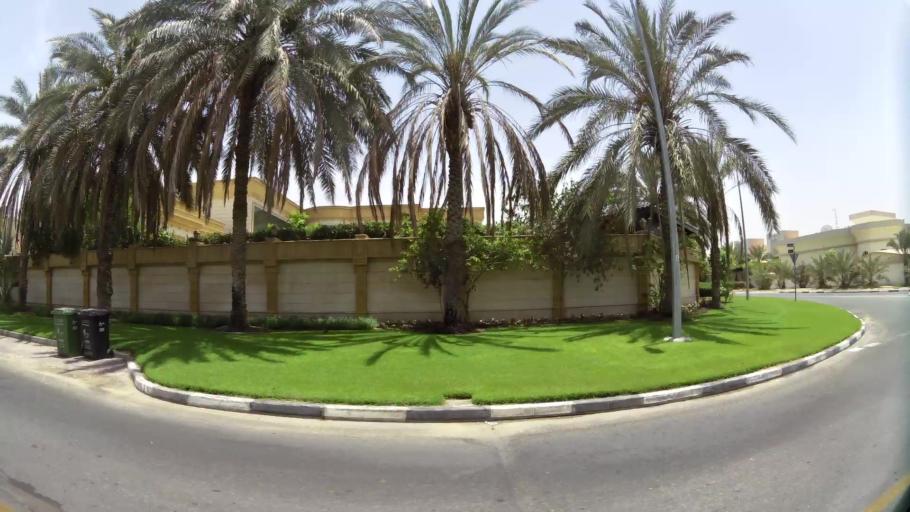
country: AE
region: Ash Shariqah
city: Sharjah
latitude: 25.2480
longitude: 55.4588
